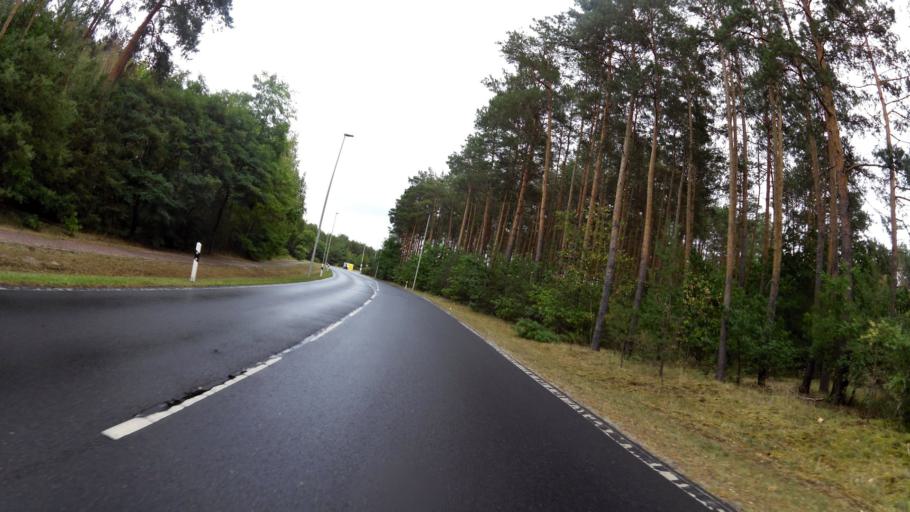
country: DE
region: Brandenburg
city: Cottbus
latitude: 51.7831
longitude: 14.3120
